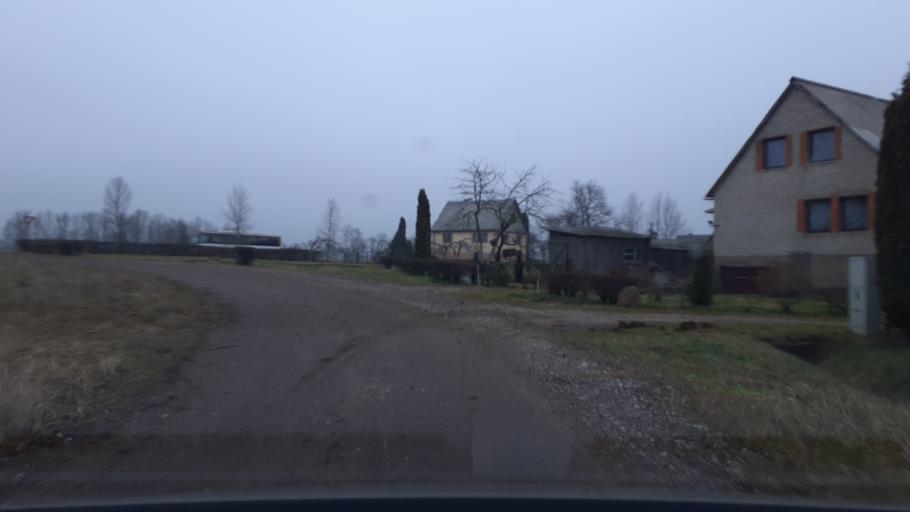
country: LV
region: Talsu Rajons
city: Sabile
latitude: 56.9556
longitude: 22.3992
